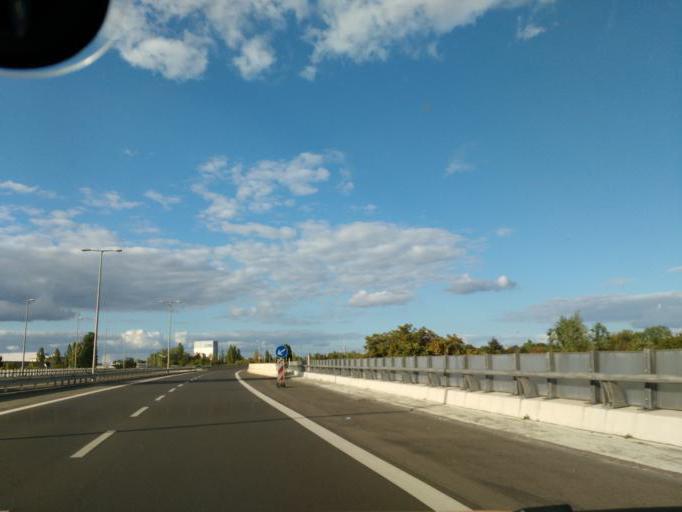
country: DE
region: Berlin
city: Tempelhof Bezirk
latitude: 52.4568
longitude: 13.4125
